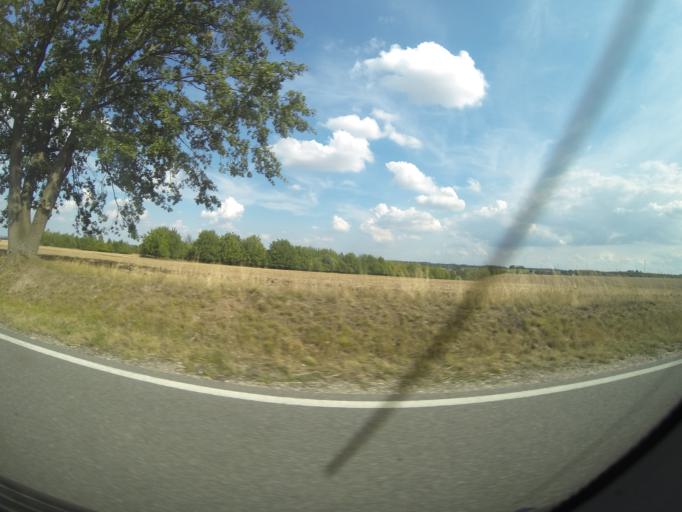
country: DE
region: Thuringia
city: Vollmershain
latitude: 50.8676
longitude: 12.3036
